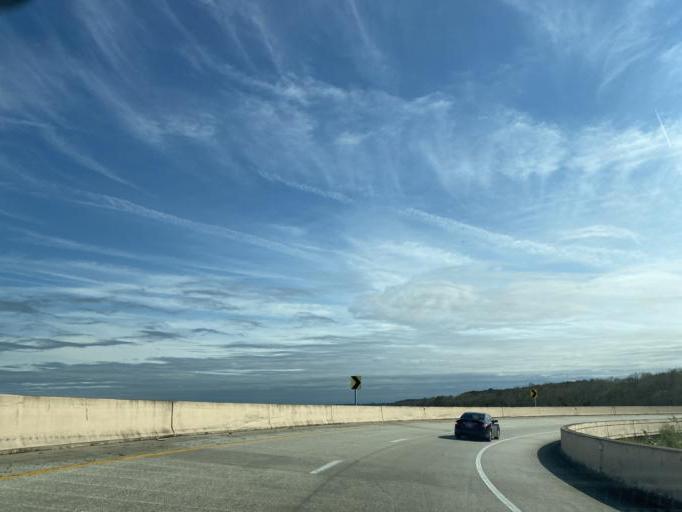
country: US
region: Florida
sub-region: Volusia County
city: DeBary
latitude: 28.8337
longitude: -81.3197
